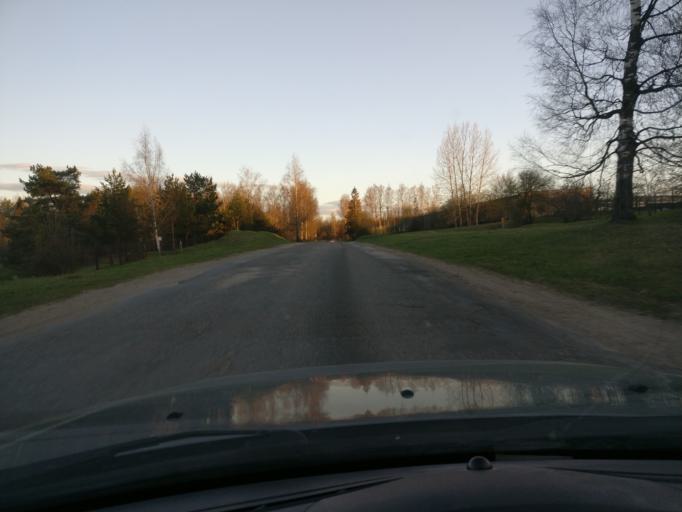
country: LV
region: Aluksnes Rajons
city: Aluksne
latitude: 57.4222
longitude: 27.0742
